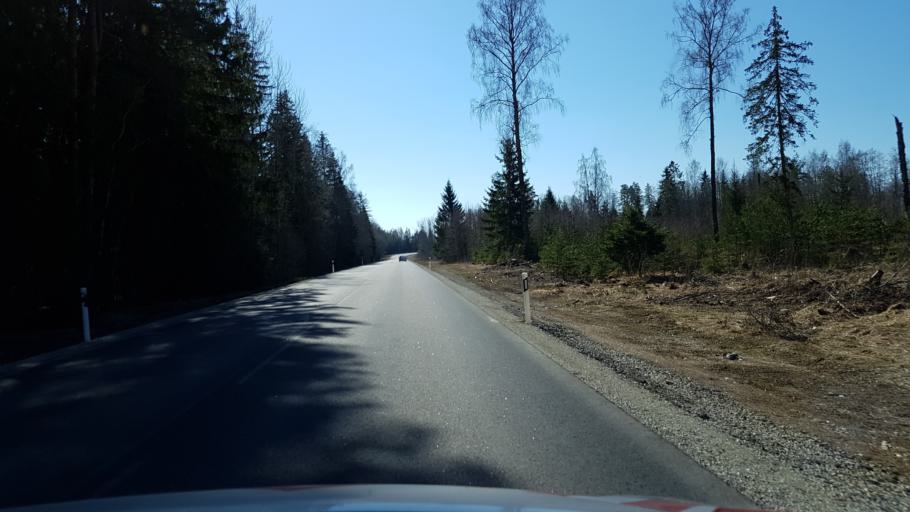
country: EE
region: Laeaene-Virumaa
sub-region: Vinni vald
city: Vinni
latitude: 59.1237
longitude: 26.6168
